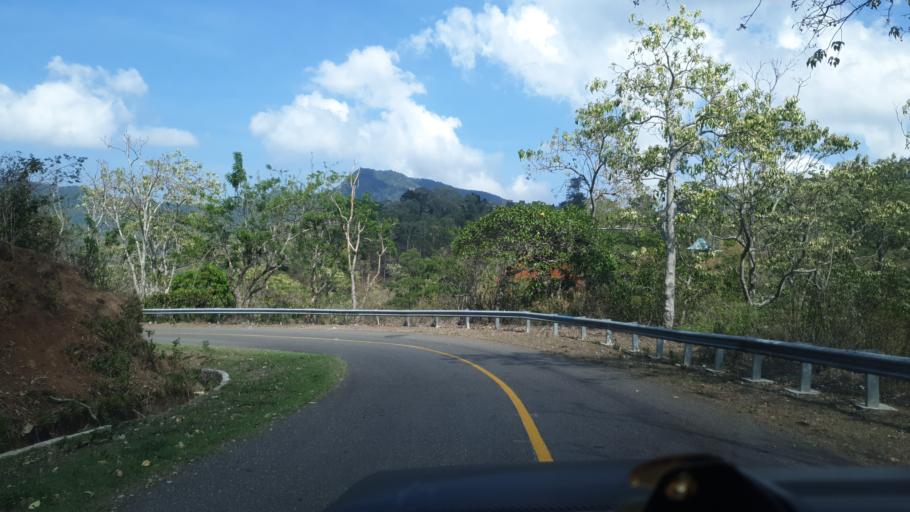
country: ID
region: East Nusa Tenggara
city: Nduaria
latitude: -8.6983
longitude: 121.8115
